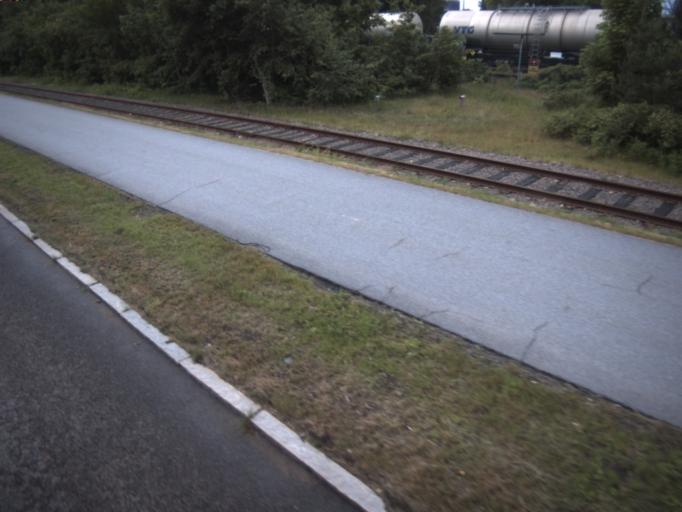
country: SE
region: Skane
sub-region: Helsingborg
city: Helsingborg
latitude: 56.0150
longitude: 12.7166
